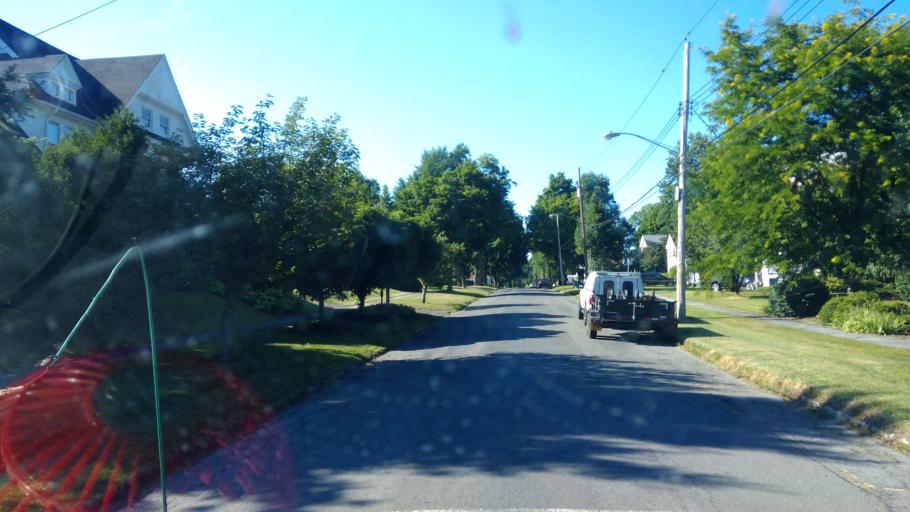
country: US
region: New York
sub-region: Wayne County
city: Lyons
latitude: 43.0672
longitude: -76.9875
